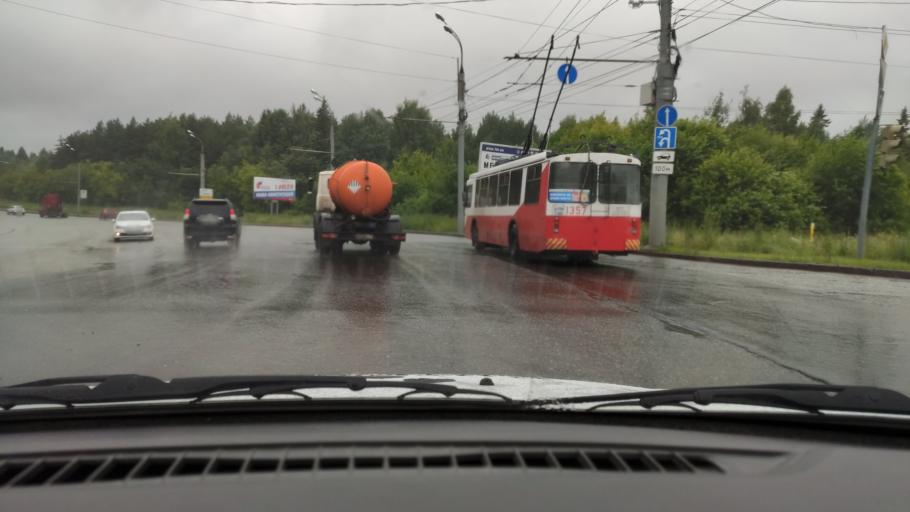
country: RU
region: Udmurtiya
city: Izhevsk
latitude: 56.8857
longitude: 53.2288
